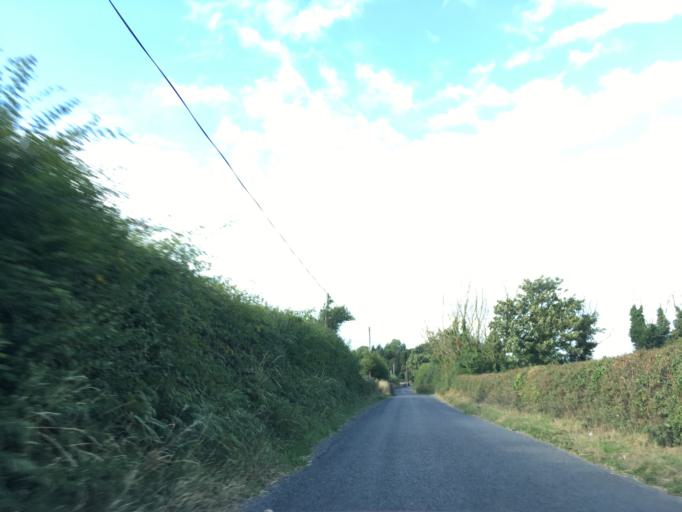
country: IE
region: Munster
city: Cahir
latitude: 52.2911
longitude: -7.9519
